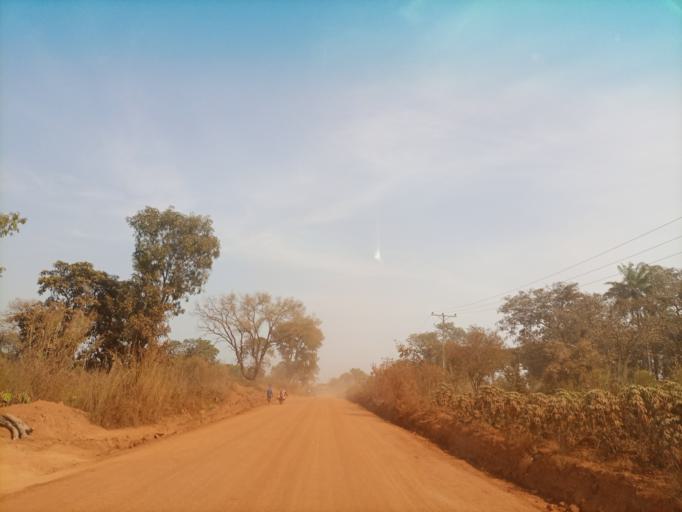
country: NG
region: Enugu
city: Eha Amufu
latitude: 6.6687
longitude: 7.7463
